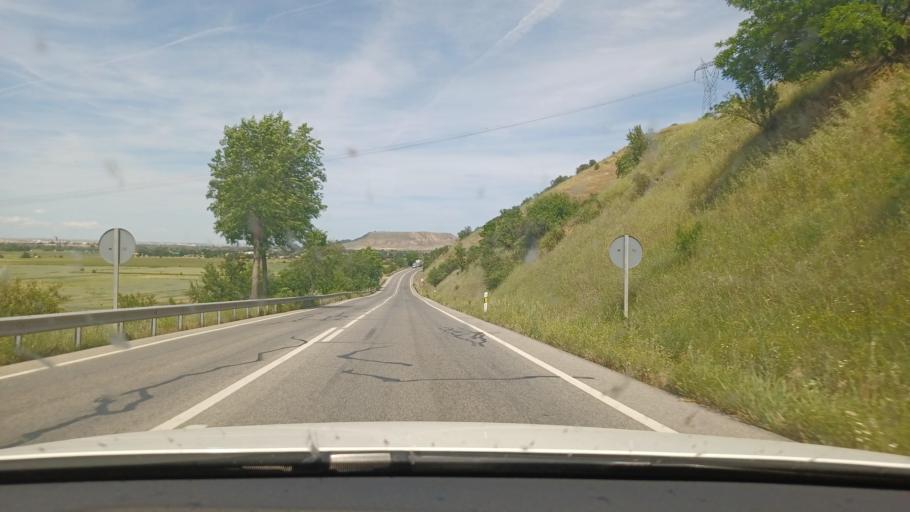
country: ES
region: Madrid
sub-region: Provincia de Madrid
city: Mejorada del Campo
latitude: 40.4174
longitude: -3.4725
